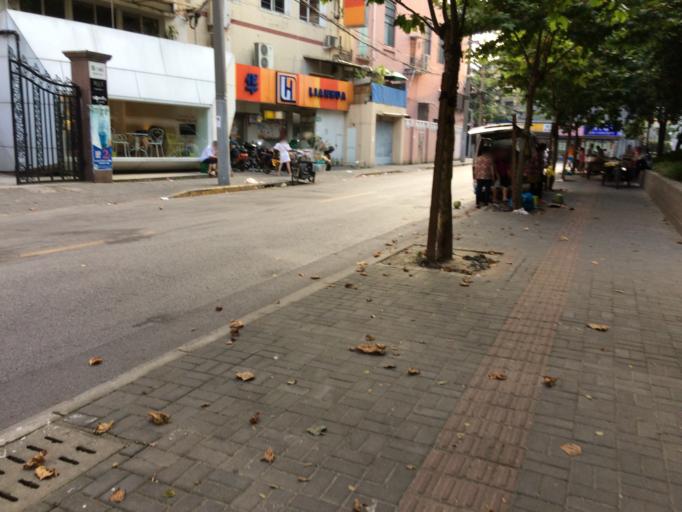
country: CN
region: Shanghai Shi
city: Changning
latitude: 31.2072
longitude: 121.4272
